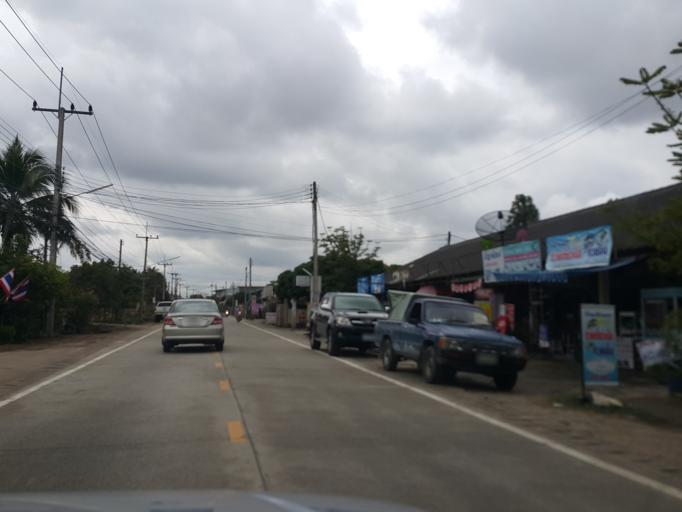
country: TH
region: Lamphun
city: Lamphun
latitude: 18.5686
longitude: 99.0653
